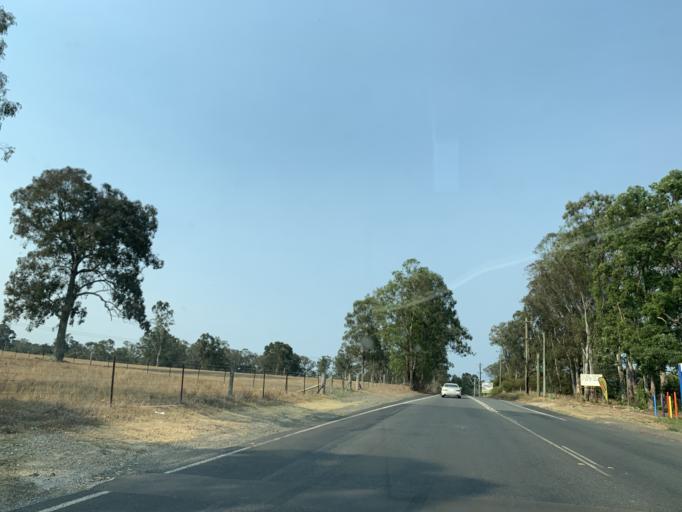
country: AU
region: New South Wales
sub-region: Blacktown
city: Rouse Hill
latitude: -33.6652
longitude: 150.9189
